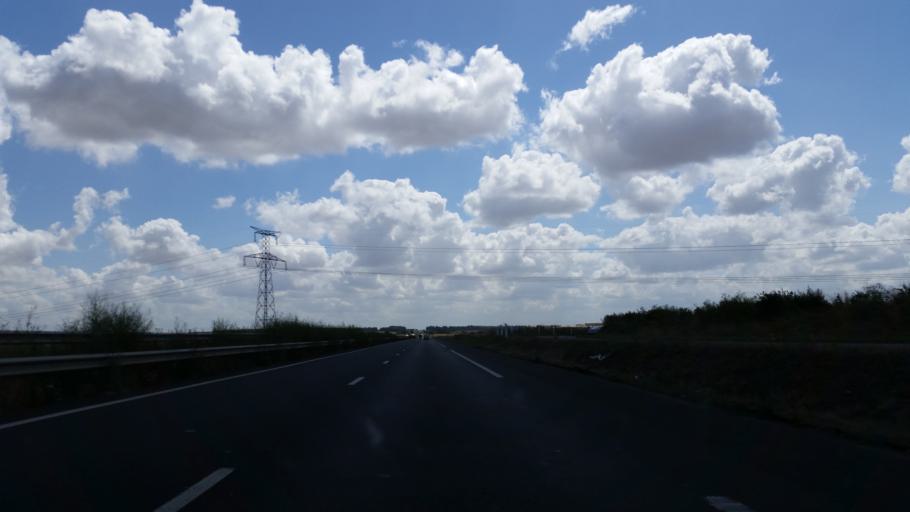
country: FR
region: Lower Normandy
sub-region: Departement du Calvados
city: Bourguebus
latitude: 49.1077
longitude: -0.3172
